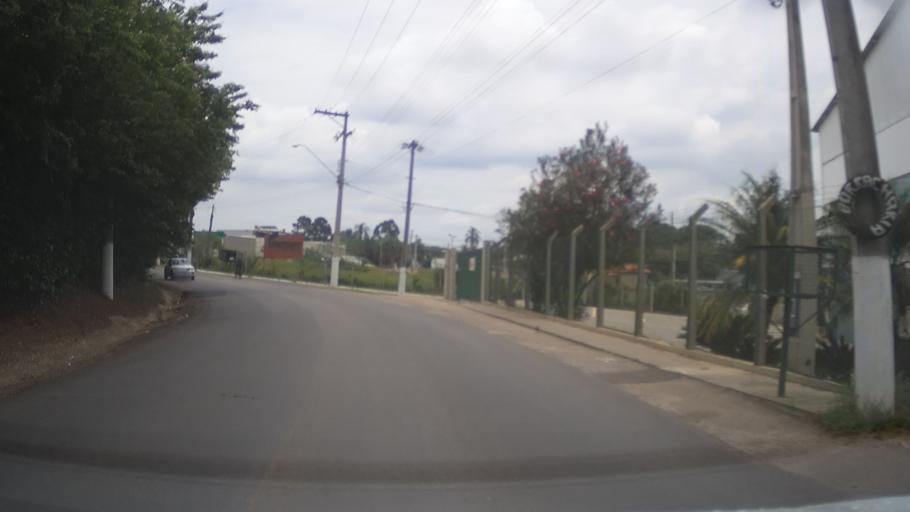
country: BR
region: Sao Paulo
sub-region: Itupeva
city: Itupeva
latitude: -23.1508
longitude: -47.0272
